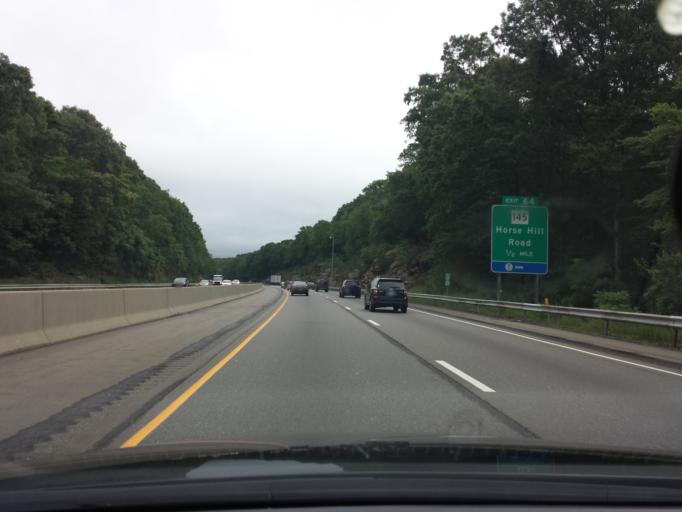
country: US
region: Connecticut
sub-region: Middlesex County
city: Clinton
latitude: 41.2895
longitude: -72.5027
